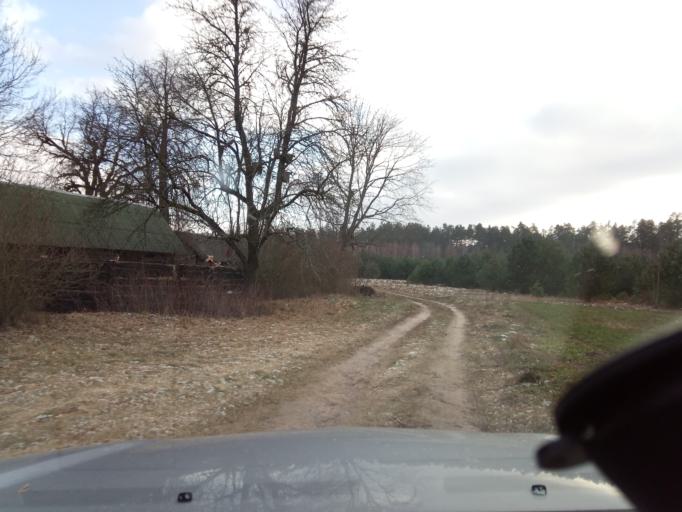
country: LT
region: Alytaus apskritis
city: Druskininkai
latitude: 54.1111
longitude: 24.2216
